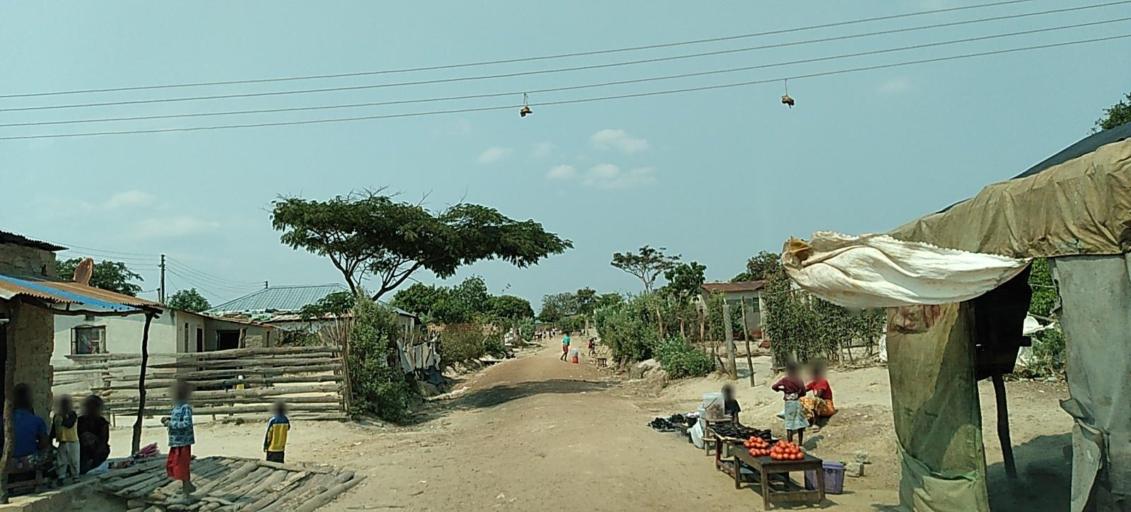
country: ZM
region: Copperbelt
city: Chambishi
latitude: -12.6262
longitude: 28.0790
